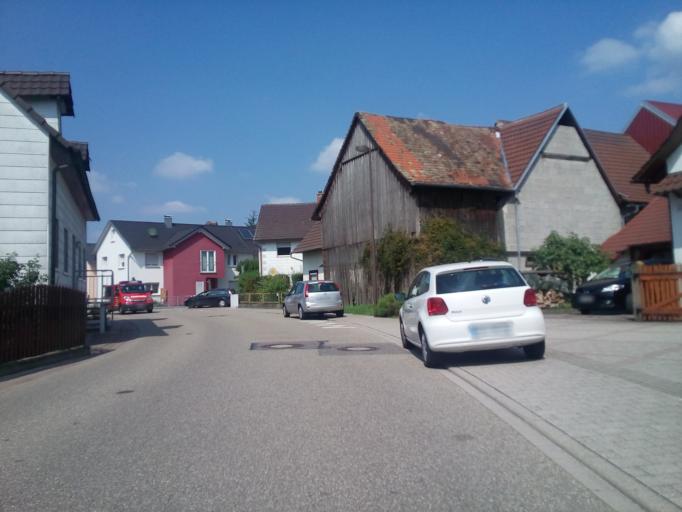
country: DE
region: Baden-Wuerttemberg
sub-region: Freiburg Region
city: Rheinau
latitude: 48.6487
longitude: 7.9287
